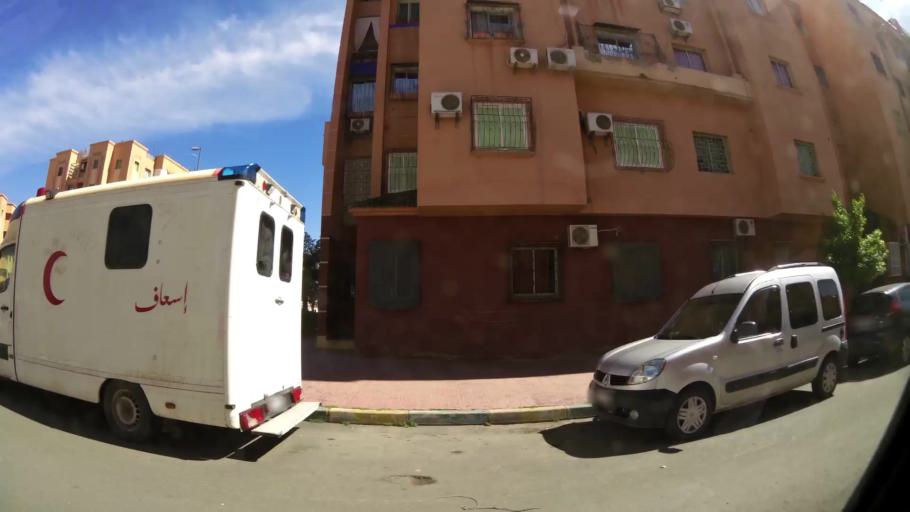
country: MA
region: Marrakech-Tensift-Al Haouz
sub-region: Marrakech
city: Marrakesh
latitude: 31.6744
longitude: -8.0172
